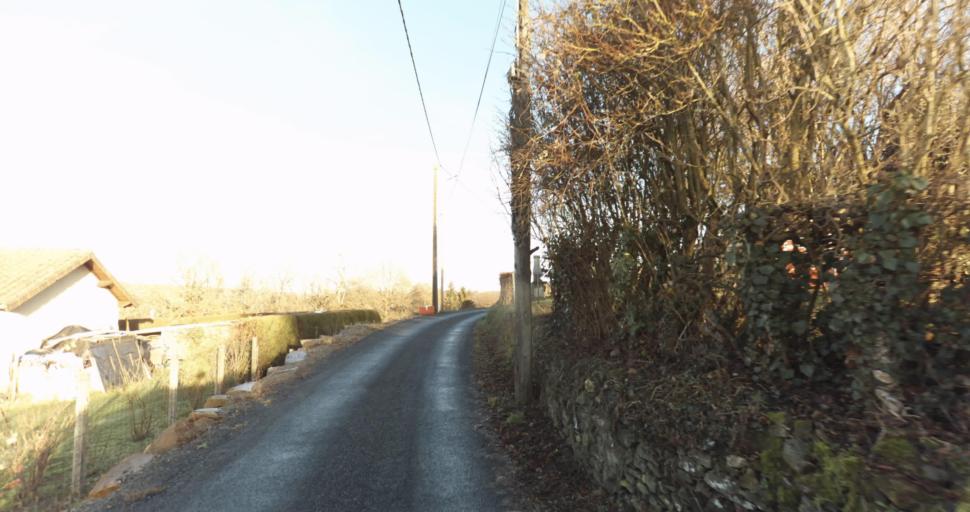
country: FR
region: Limousin
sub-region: Departement de la Haute-Vienne
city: Aixe-sur-Vienne
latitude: 45.7928
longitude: 1.1454
